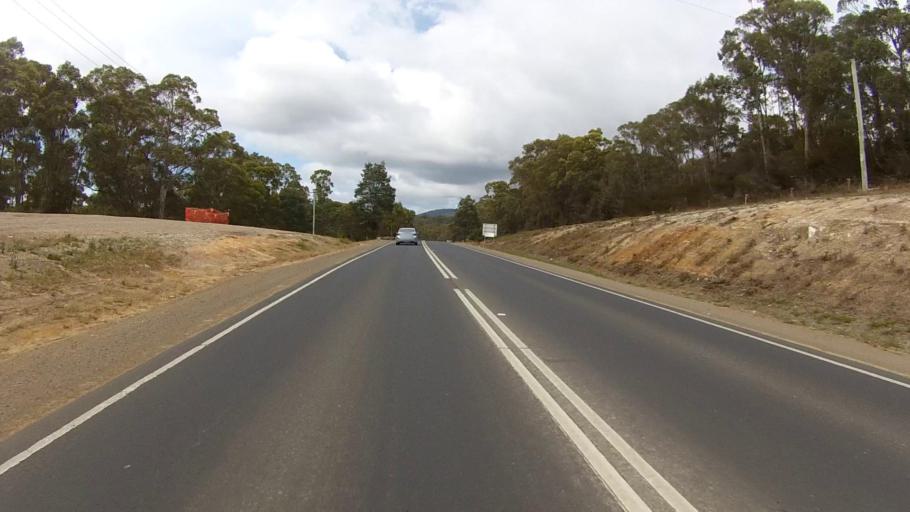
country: AU
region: Tasmania
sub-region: Kingborough
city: Margate
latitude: -43.0461
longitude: 147.2648
